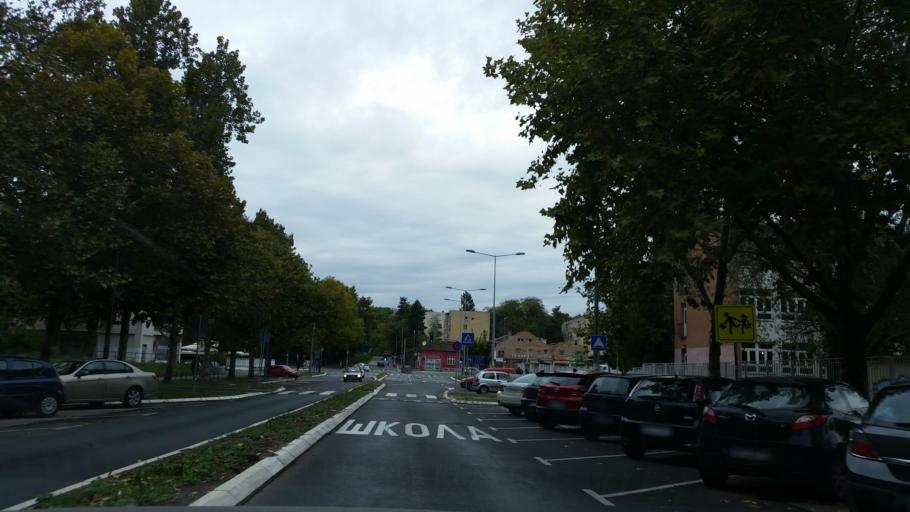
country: RS
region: Central Serbia
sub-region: Belgrade
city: Zemun
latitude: 44.8068
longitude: 20.3773
